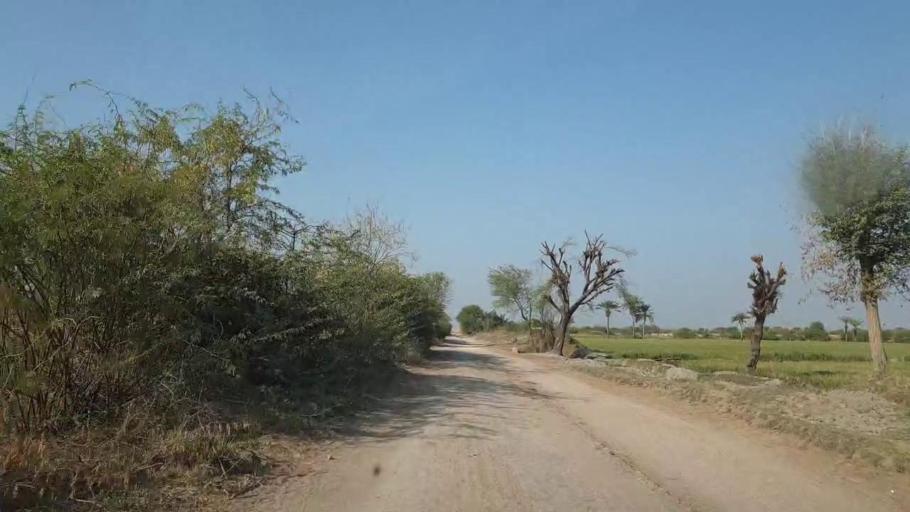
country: PK
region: Sindh
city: Tando Mittha Khan
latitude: 25.7687
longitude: 69.1936
